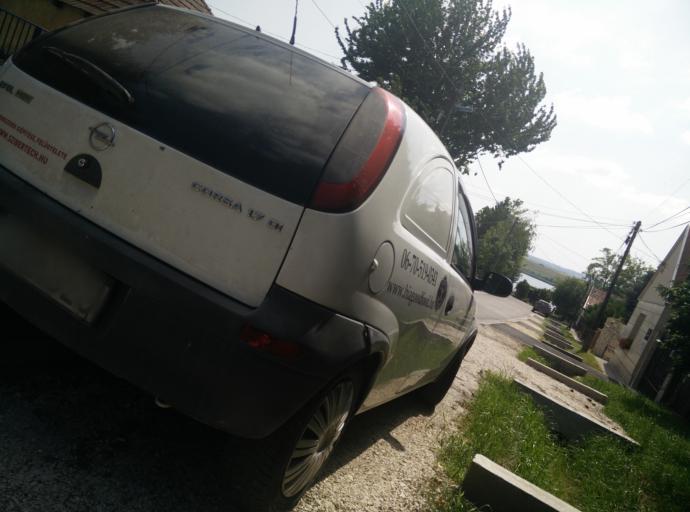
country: HU
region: Pest
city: Biatorbagy
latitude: 47.4673
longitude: 18.8051
